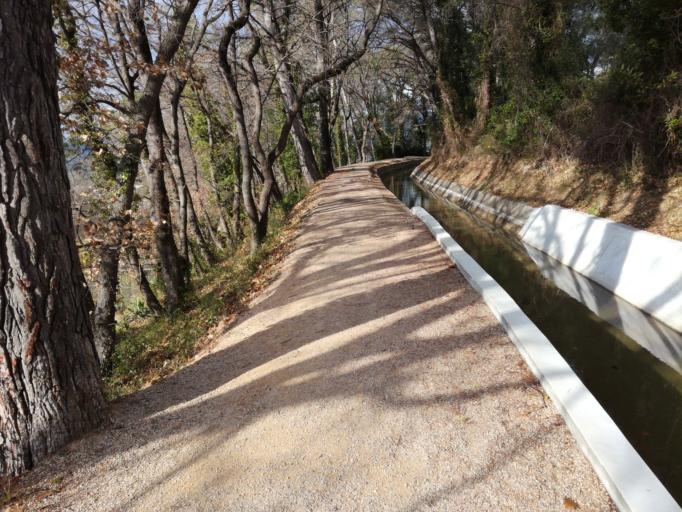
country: FR
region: Provence-Alpes-Cote d'Azur
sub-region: Departement des Alpes-Maritimes
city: Mouans-Sartoux
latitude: 43.6141
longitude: 6.9832
